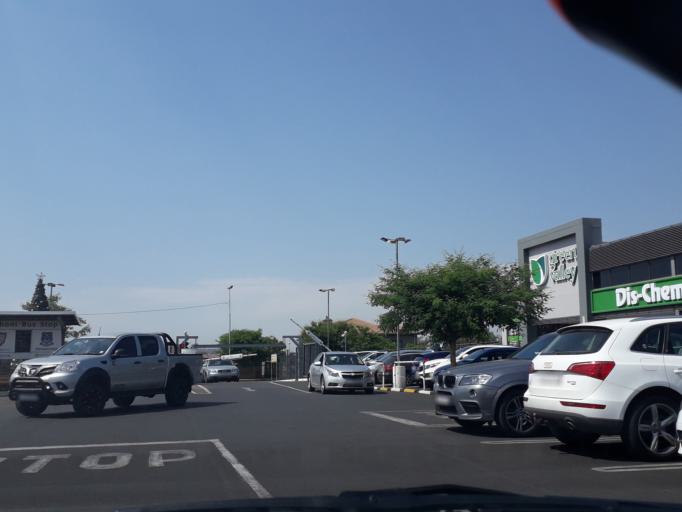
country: ZA
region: Gauteng
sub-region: City of Johannesburg Metropolitan Municipality
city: Modderfontein
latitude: -26.1179
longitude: 28.1563
